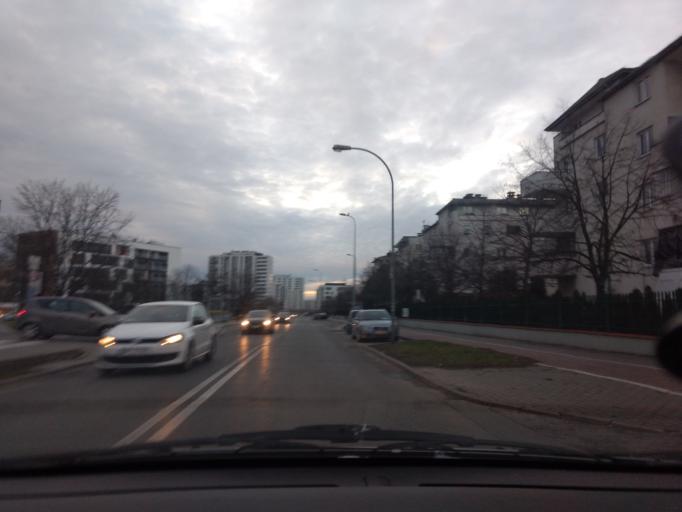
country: PL
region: Masovian Voivodeship
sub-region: Warszawa
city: Praga Poludnie
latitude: 52.2306
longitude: 21.0849
